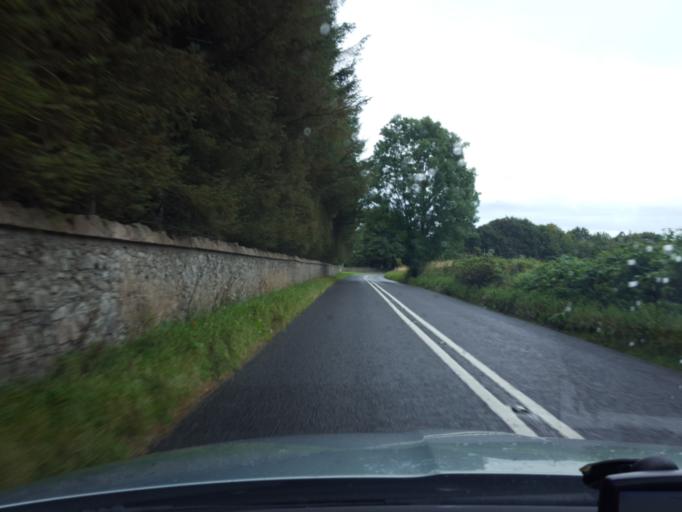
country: GB
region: Scotland
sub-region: Aberdeenshire
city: Stonehaven
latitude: 56.9800
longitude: -2.2454
